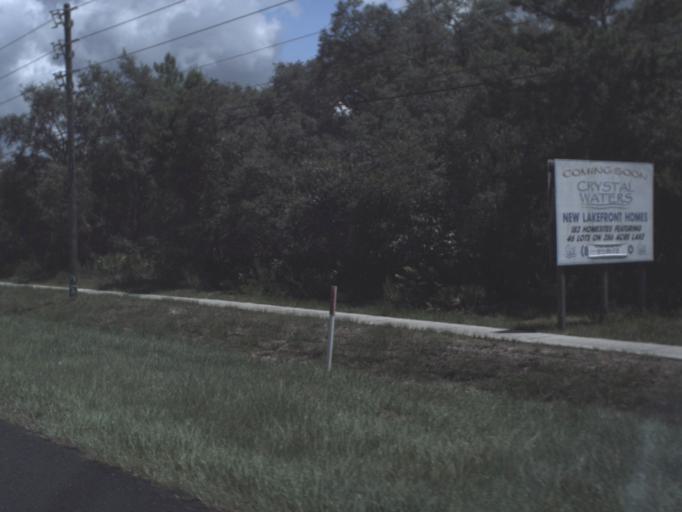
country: US
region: Florida
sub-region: Hernando County
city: North Weeki Wachee
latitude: 28.5732
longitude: -82.5573
